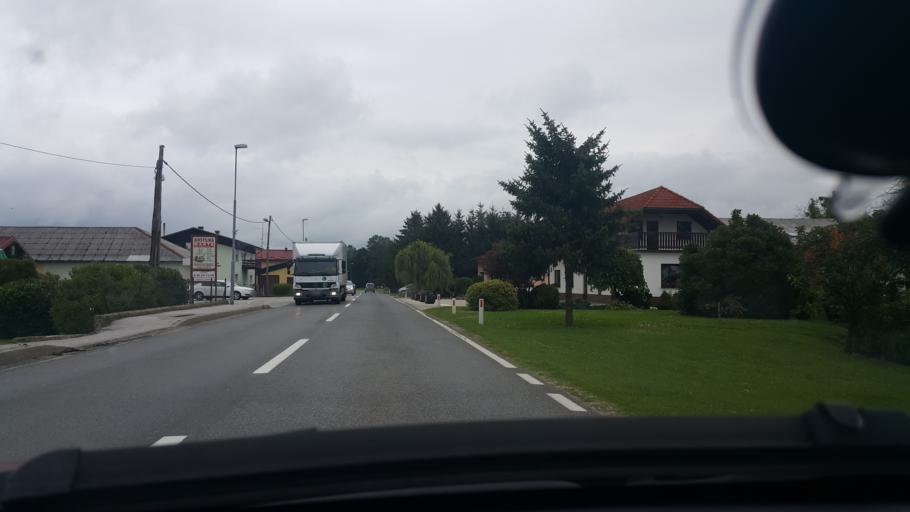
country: SI
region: Zavrc
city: Zavrc
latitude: 46.4139
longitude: 16.0649
